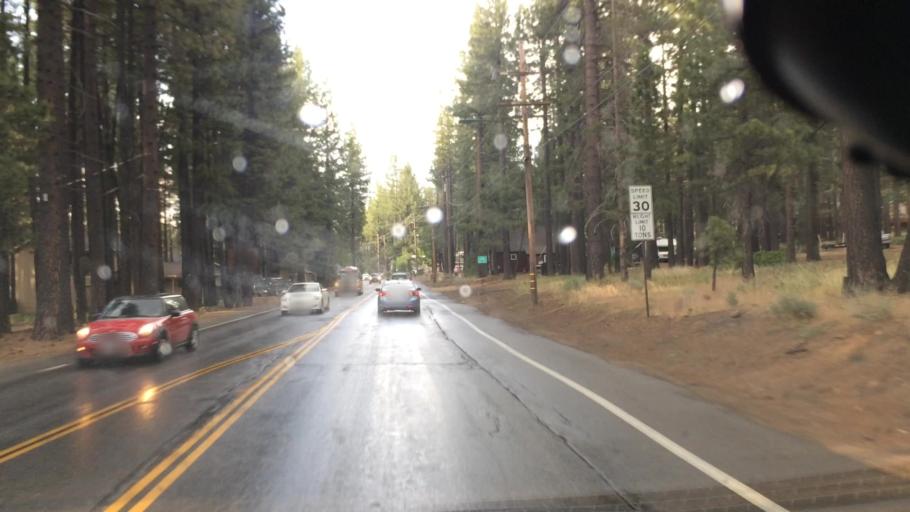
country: US
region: California
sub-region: El Dorado County
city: South Lake Tahoe
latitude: 38.9417
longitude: -119.9518
